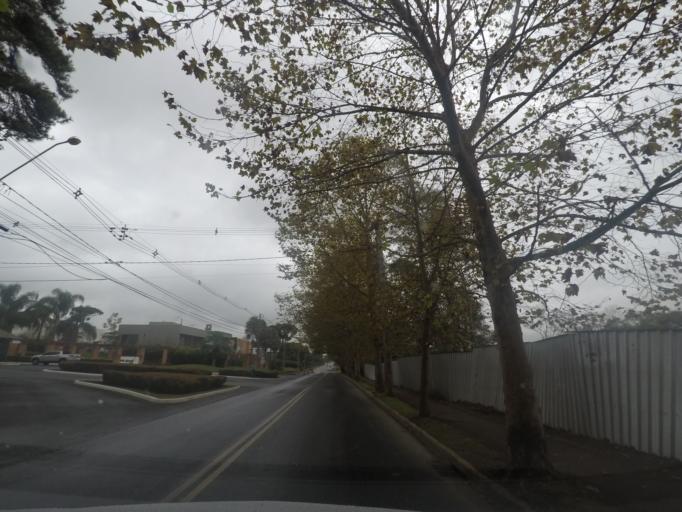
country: BR
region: Parana
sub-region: Pinhais
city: Pinhais
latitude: -25.3906
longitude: -49.1546
